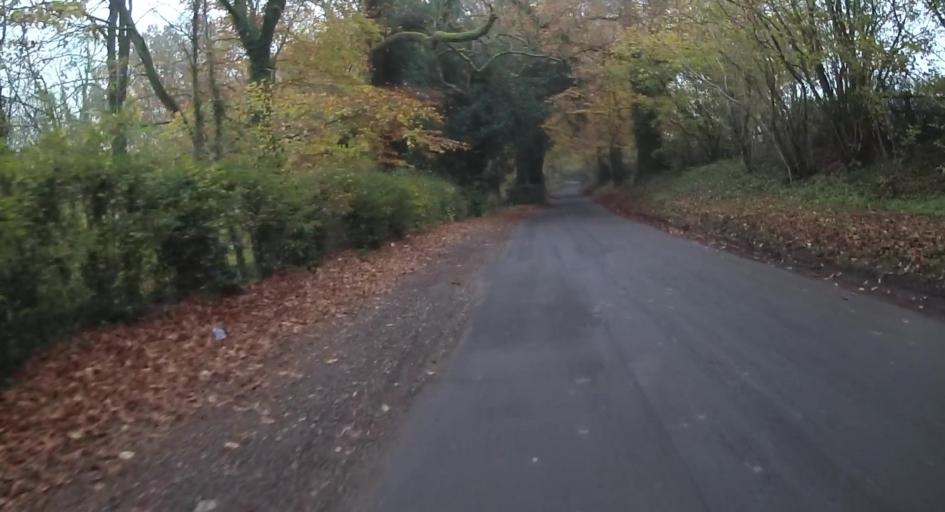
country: GB
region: England
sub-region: Hampshire
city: Alton
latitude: 51.1841
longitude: -0.9754
